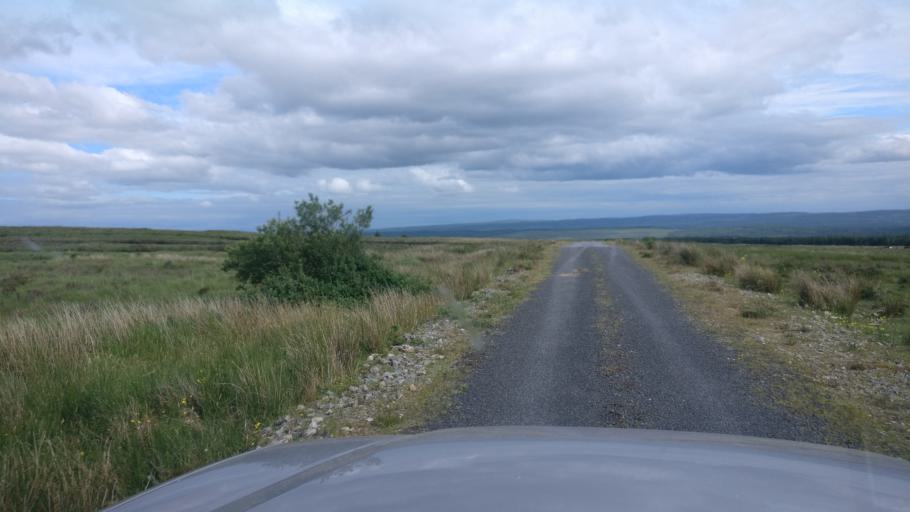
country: IE
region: Connaught
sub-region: County Galway
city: Gort
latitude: 53.0787
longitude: -8.6831
